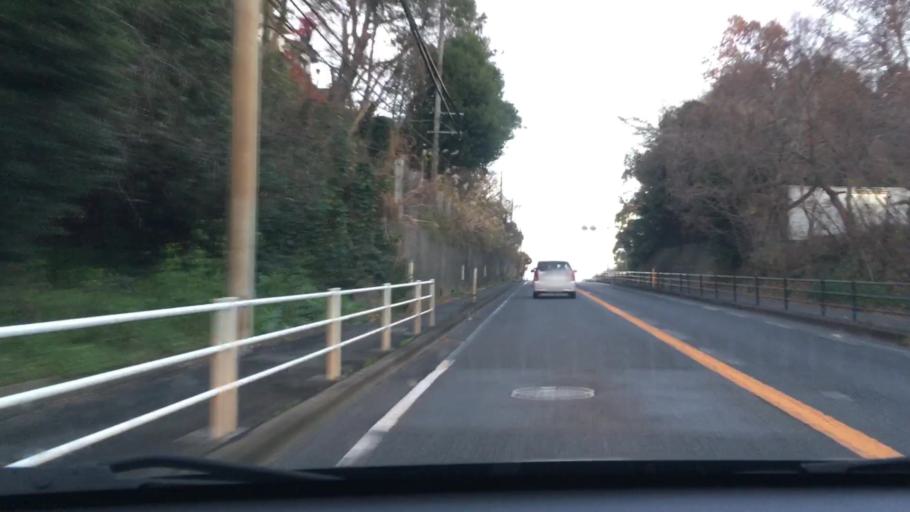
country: JP
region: Fukuoka
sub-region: Buzen-shi
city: Buzen
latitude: 33.6194
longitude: 131.0964
